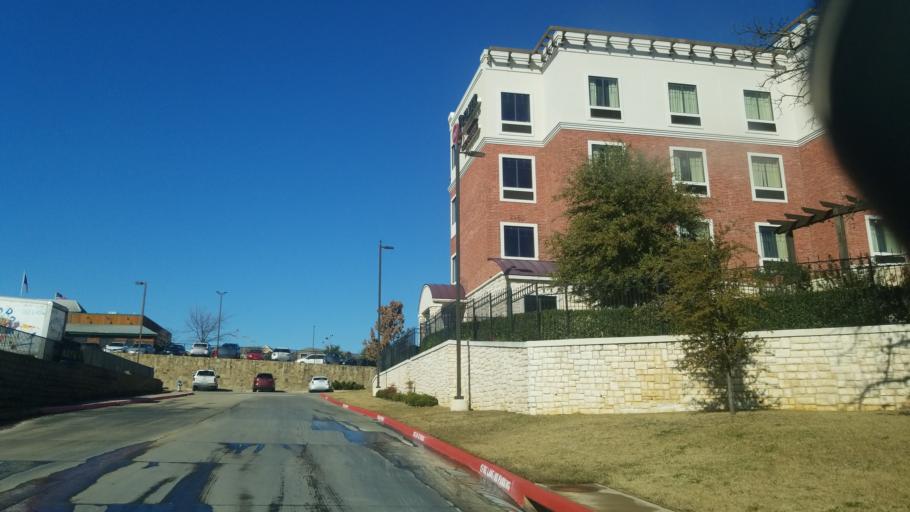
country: US
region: Texas
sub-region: Denton County
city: Corinth
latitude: 33.1823
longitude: -97.1000
